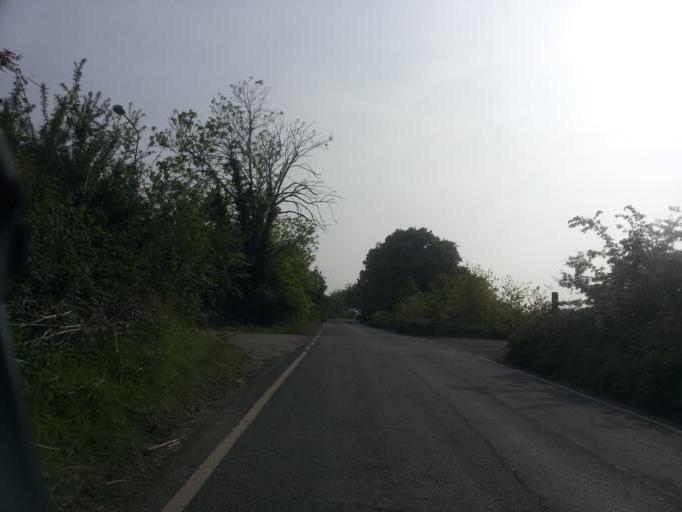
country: GB
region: England
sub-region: Kent
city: Newington
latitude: 51.3791
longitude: 0.6935
